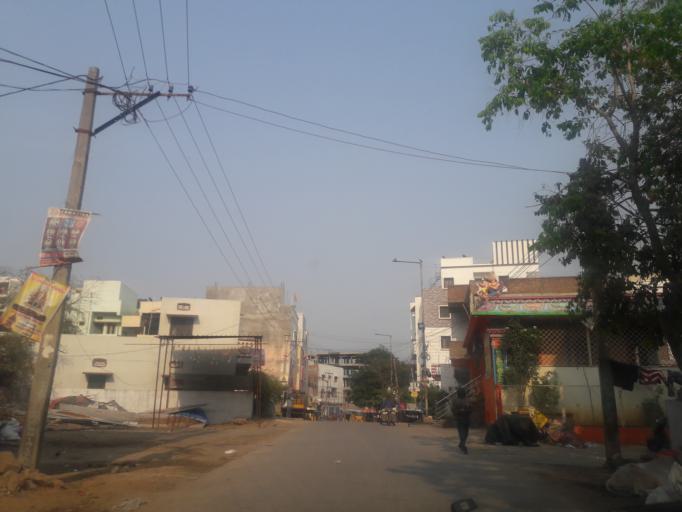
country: IN
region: Telangana
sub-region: Rangareddi
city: Uppal Kalan
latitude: 17.4113
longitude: 78.5655
